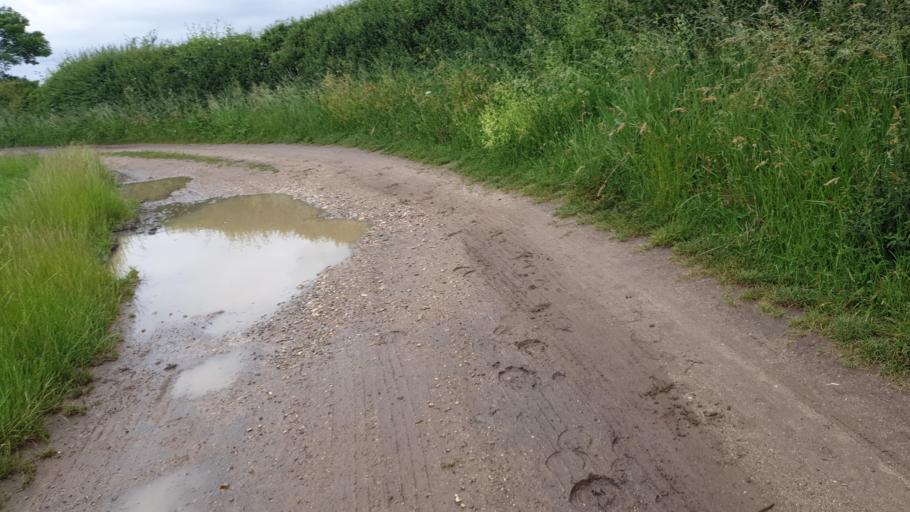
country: GB
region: England
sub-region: Essex
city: Great Bentley
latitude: 51.8826
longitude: 1.0622
